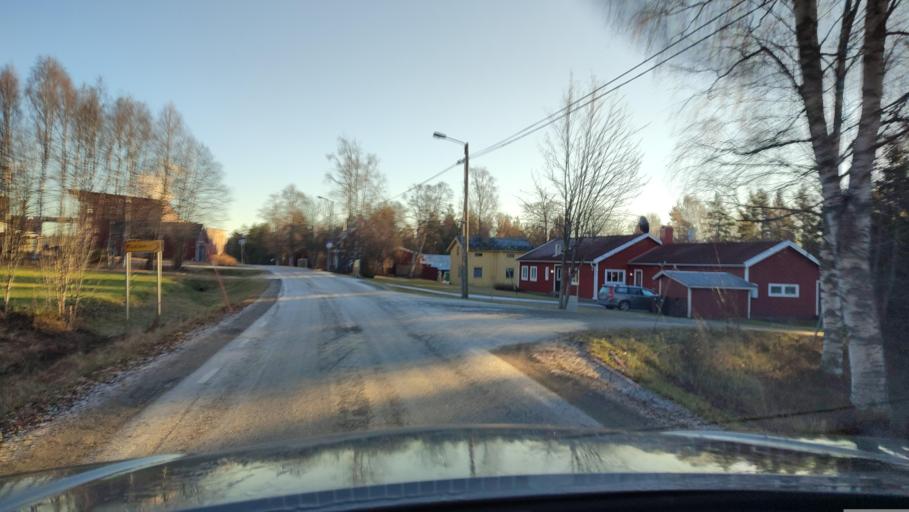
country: SE
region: Vaesterbotten
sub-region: Skelleftea Kommun
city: Viken
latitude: 64.7019
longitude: 20.9005
